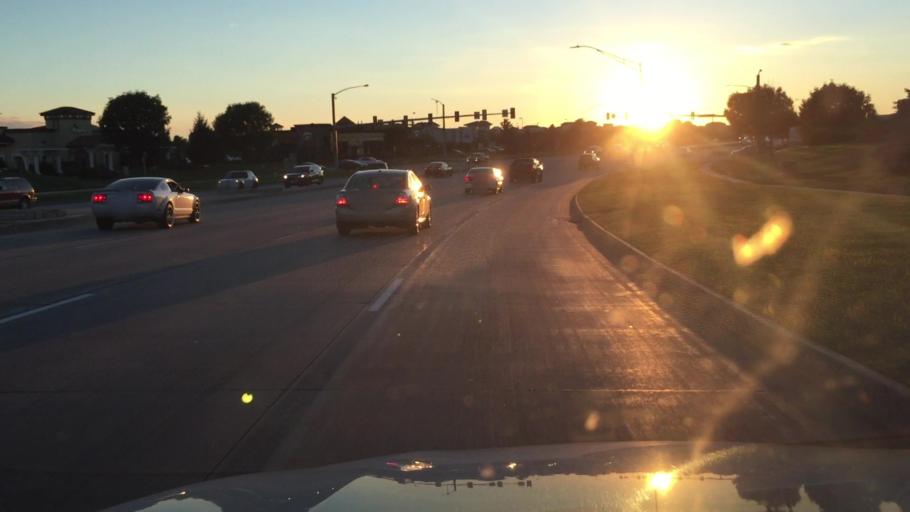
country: US
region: Iowa
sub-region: Polk County
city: Clive
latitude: 41.5591
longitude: -93.7929
